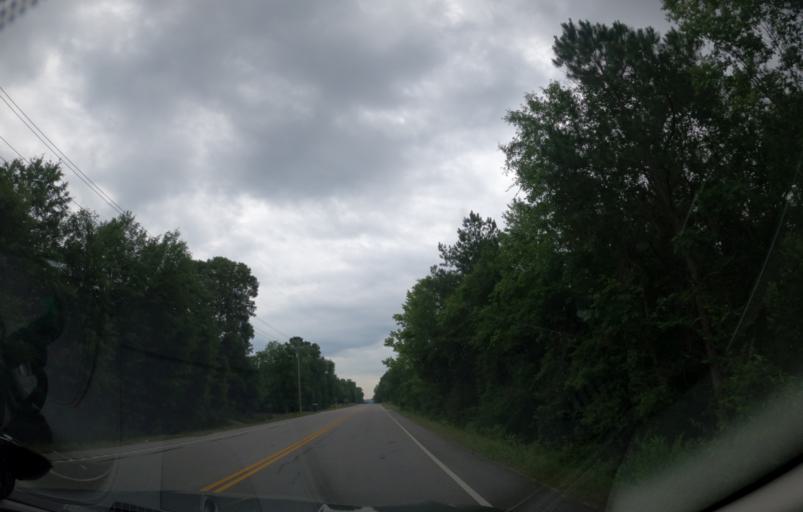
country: US
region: South Carolina
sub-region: Aiken County
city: Aiken
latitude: 33.5661
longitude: -81.6148
